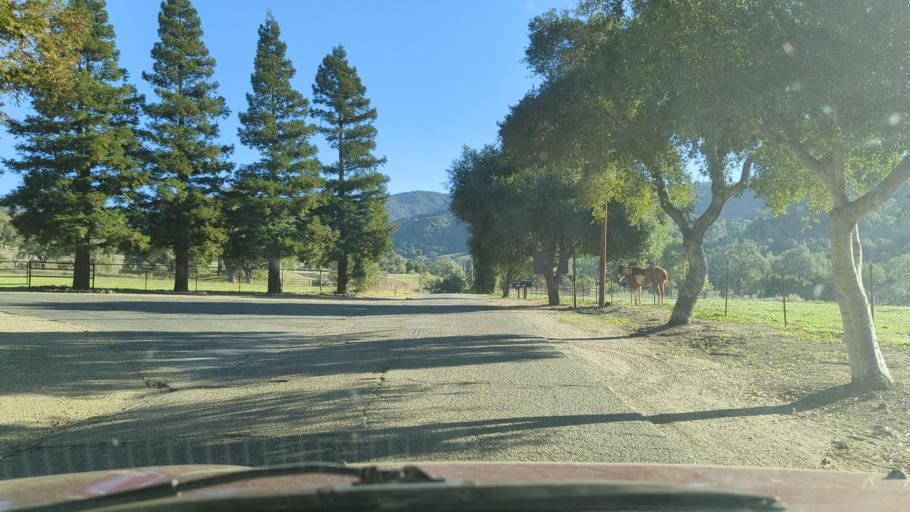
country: US
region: California
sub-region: Santa Barbara County
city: Santa Ynez
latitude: 34.5752
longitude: -120.0982
